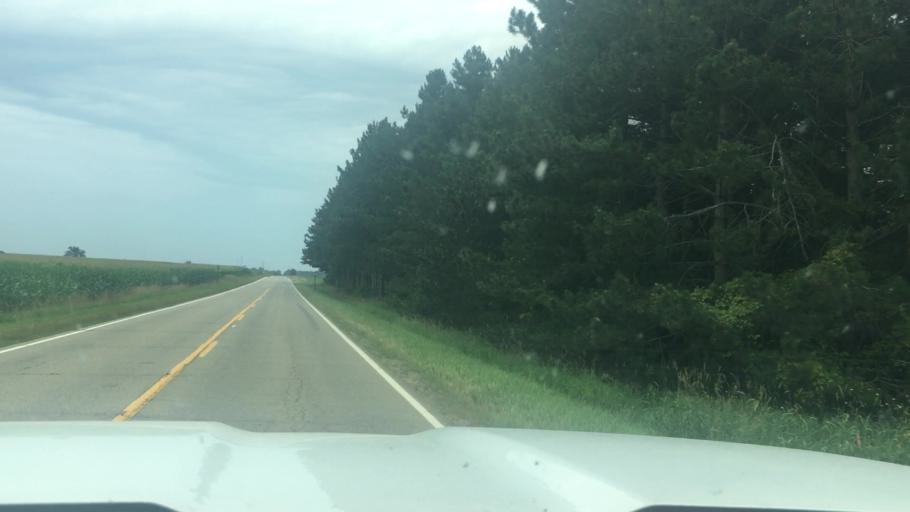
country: US
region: Michigan
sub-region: Clinton County
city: Saint Johns
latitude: 43.0279
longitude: -84.4842
